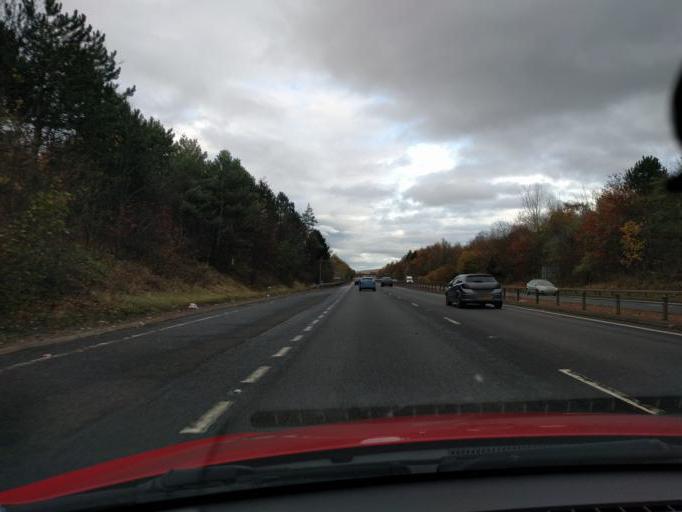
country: GB
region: Scotland
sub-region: East Lothian
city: Musselburgh
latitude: 55.9250
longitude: -3.0493
